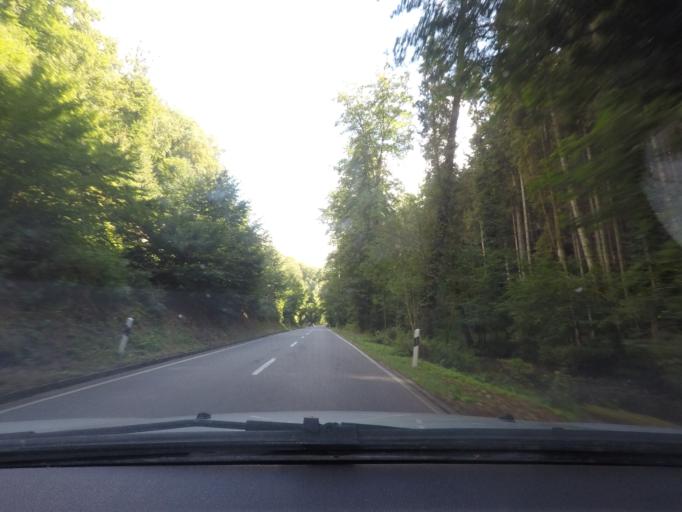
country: LU
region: Grevenmacher
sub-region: Canton d'Echternach
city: Waldbillig
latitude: 49.7599
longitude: 6.2767
